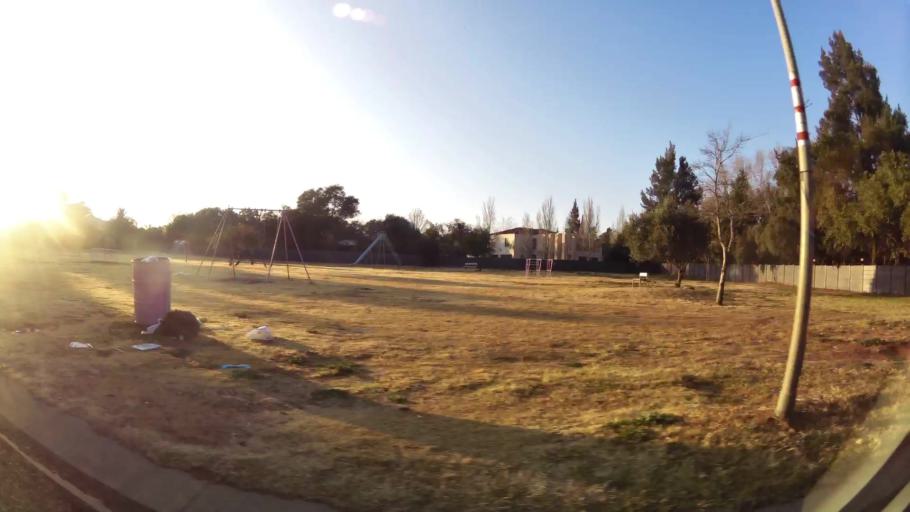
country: ZA
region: Orange Free State
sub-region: Mangaung Metropolitan Municipality
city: Bloemfontein
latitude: -29.0848
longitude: 26.1564
